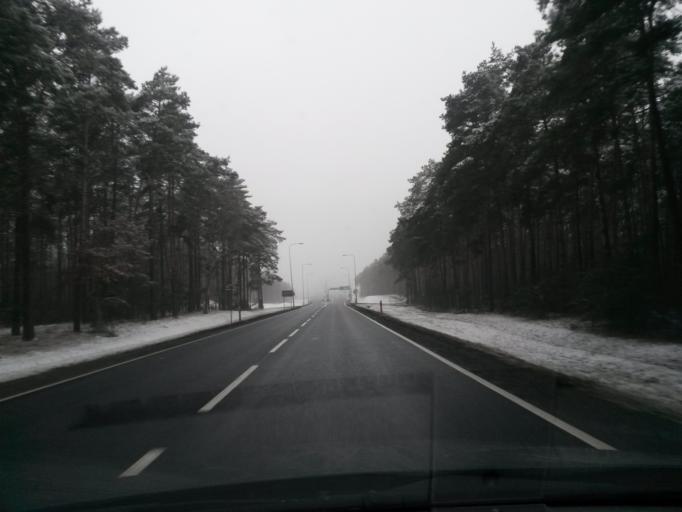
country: PL
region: Kujawsko-Pomorskie
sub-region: Bydgoszcz
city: Bydgoszcz
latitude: 53.0507
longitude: 18.0118
